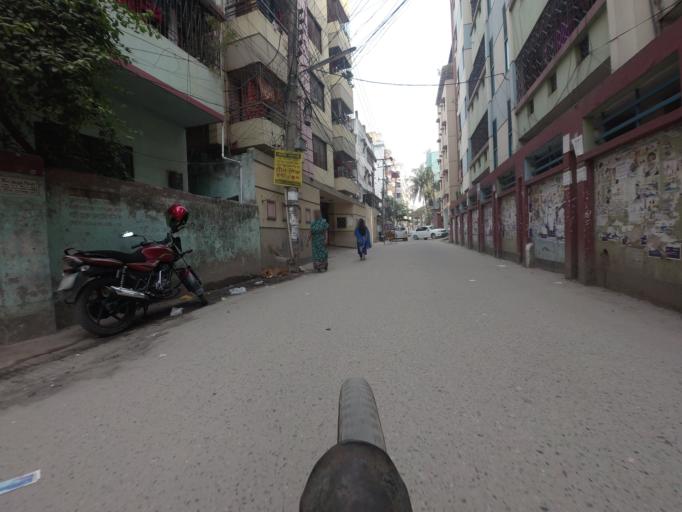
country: BD
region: Dhaka
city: Azimpur
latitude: 23.7729
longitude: 90.3559
